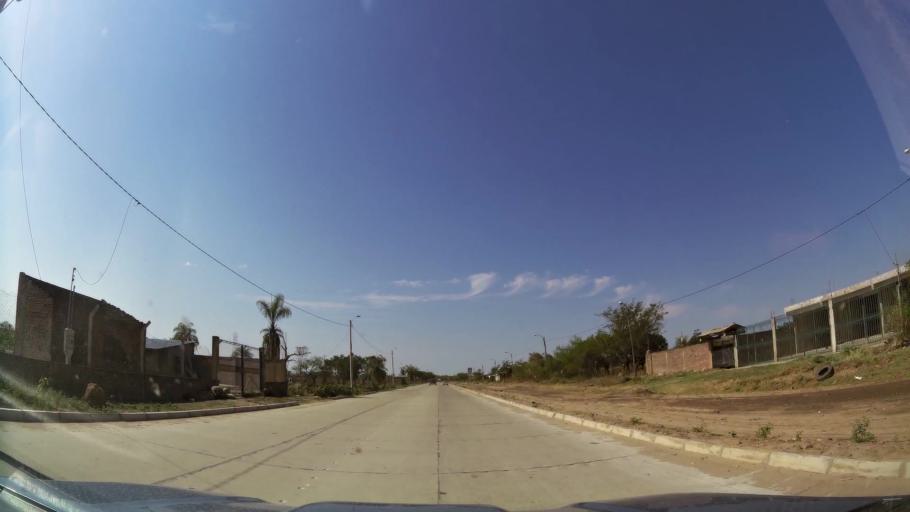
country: BO
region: Santa Cruz
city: Cotoca
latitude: -17.7148
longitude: -63.0688
